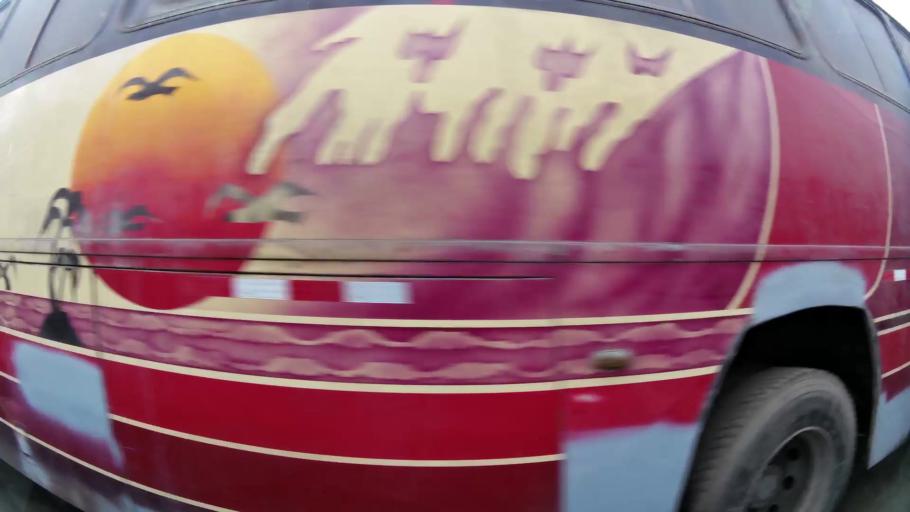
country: PE
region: Lima
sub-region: Lima
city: Independencia
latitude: -11.9942
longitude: -77.0062
